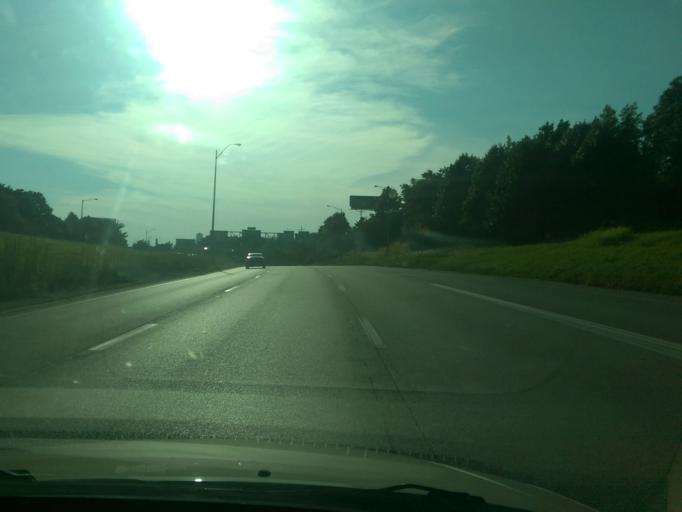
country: US
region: Missouri
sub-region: Jackson County
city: Kansas City
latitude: 39.0967
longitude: -94.5457
